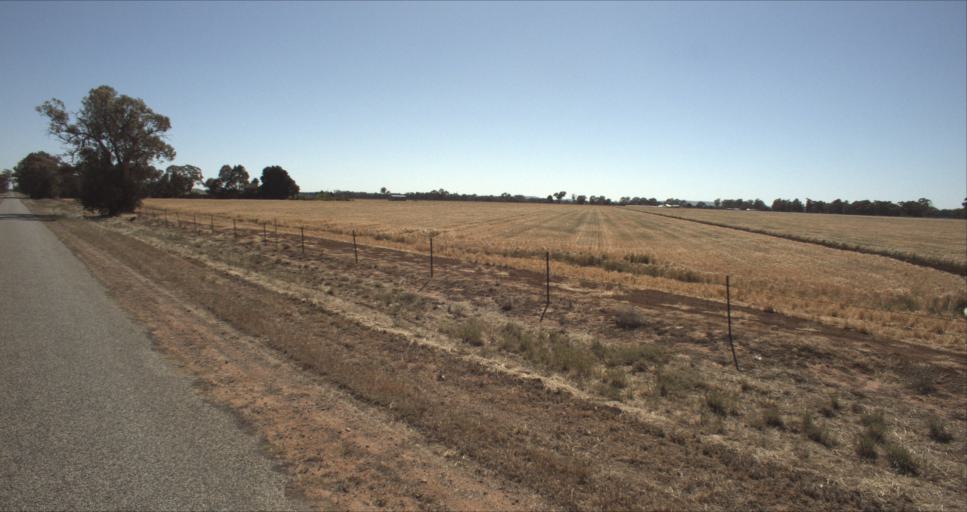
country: AU
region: New South Wales
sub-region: Leeton
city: Leeton
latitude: -34.5473
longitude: 146.3153
